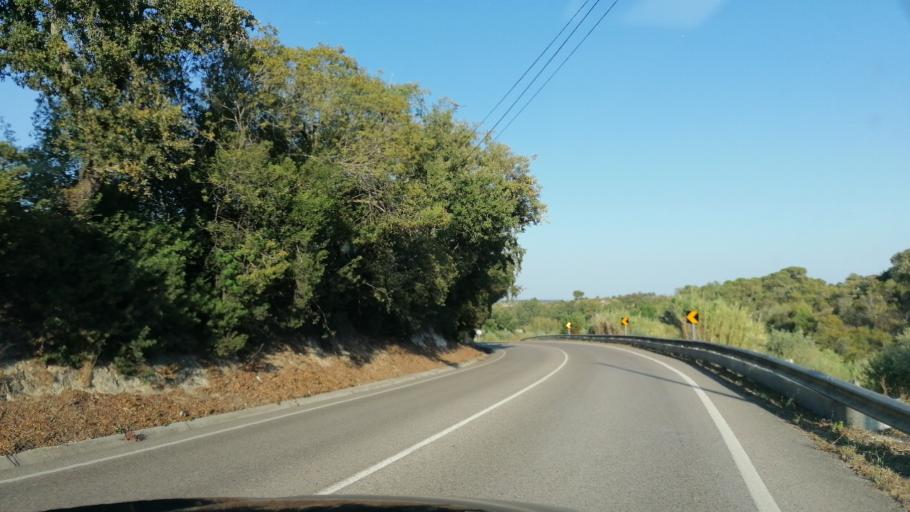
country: PT
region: Santarem
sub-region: Alcanena
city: Alcanena
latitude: 39.3558
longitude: -8.6607
